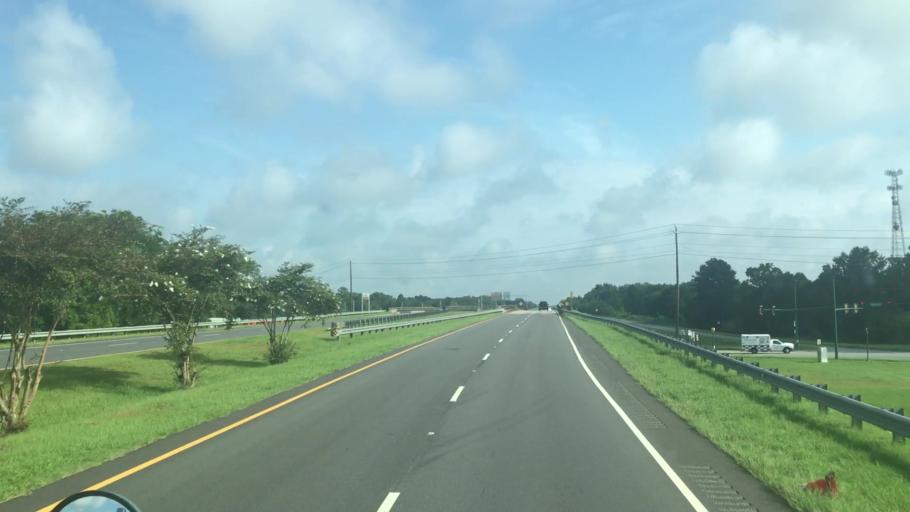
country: US
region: Georgia
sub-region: Decatur County
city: Bainbridge
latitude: 30.9181
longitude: -84.6004
